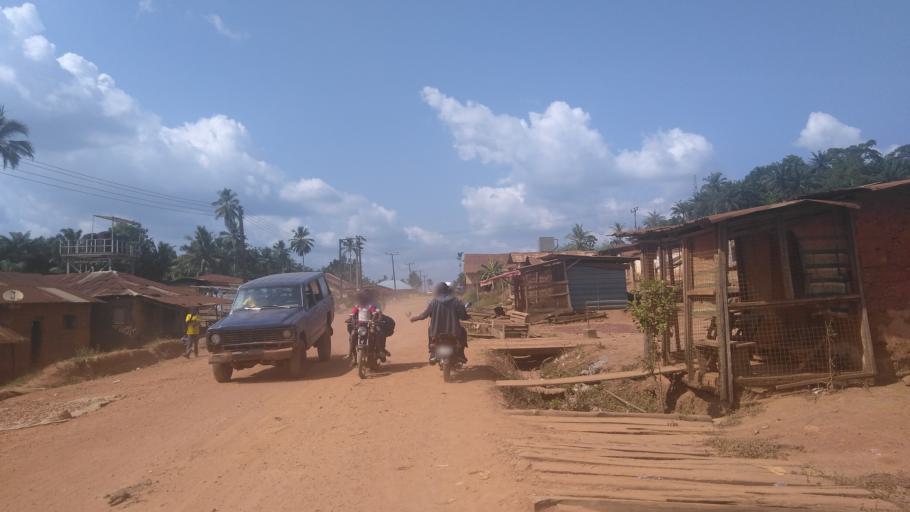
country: NG
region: Osun
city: Ifetedo
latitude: 7.0156
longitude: 4.6334
